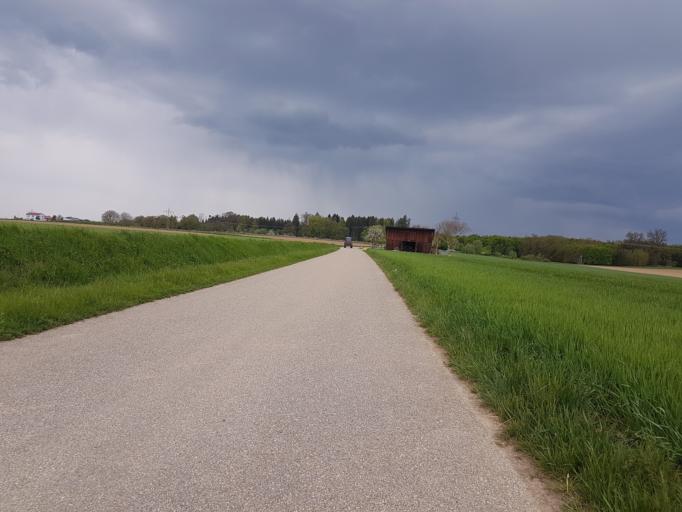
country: DE
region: Baden-Wuerttemberg
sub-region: Regierungsbezirk Stuttgart
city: Bondorf
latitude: 48.5176
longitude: 8.8096
